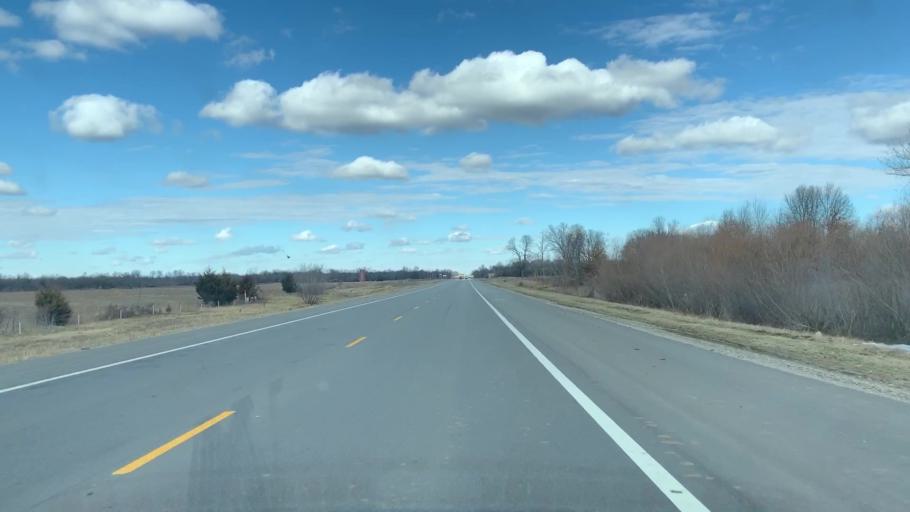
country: US
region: Kansas
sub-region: Cherokee County
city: Columbus
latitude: 37.2638
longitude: -94.8321
